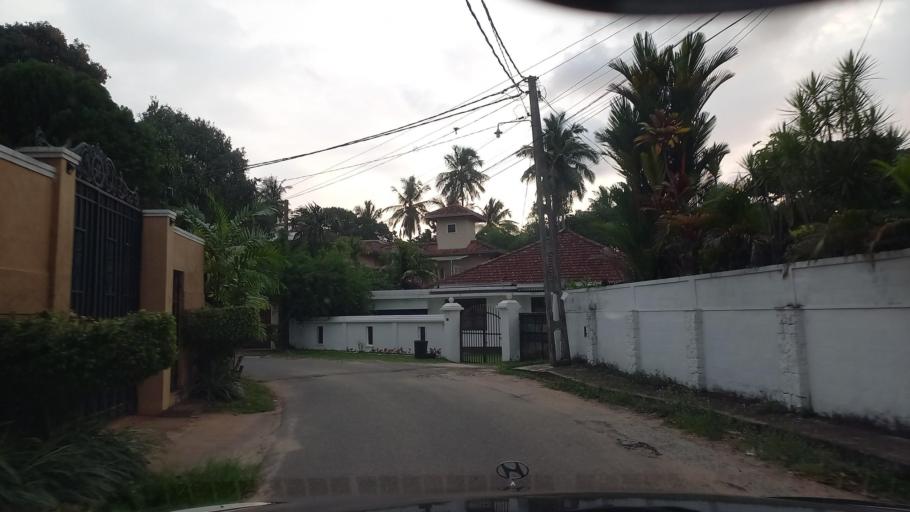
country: LK
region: Western
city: Battaramulla South
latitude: 6.8968
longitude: 79.9160
